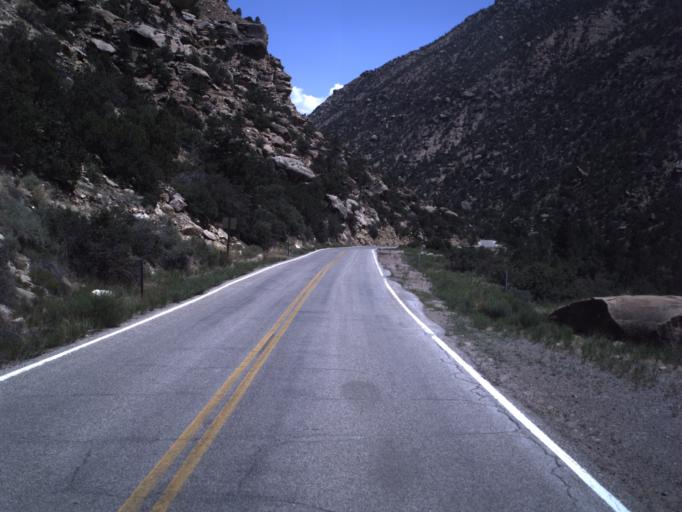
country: US
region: Utah
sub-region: Emery County
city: Orangeville
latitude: 39.2746
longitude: -111.2056
